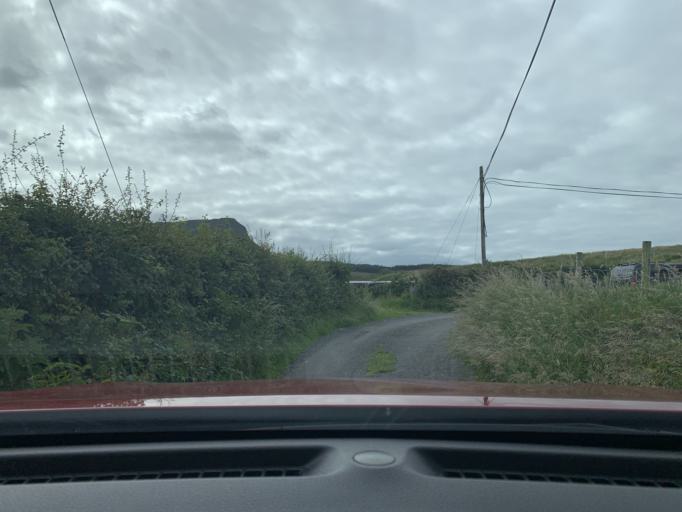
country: IE
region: Connaught
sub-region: Sligo
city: Sligo
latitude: 54.3774
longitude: -8.5199
